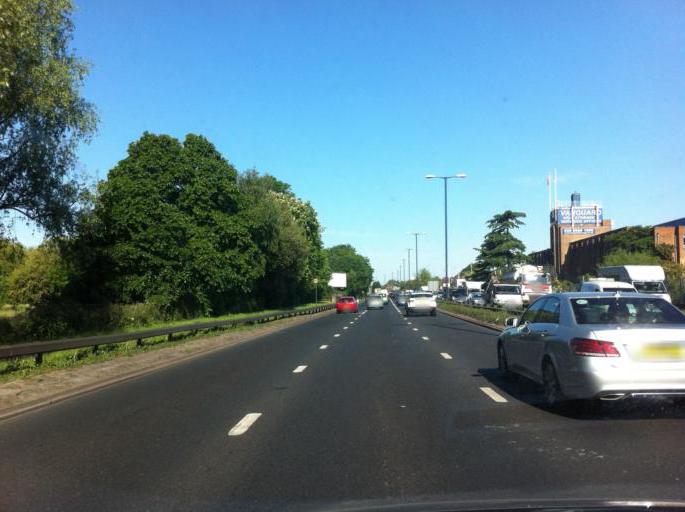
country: GB
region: England
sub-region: Greater London
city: Ealing Broadway
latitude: 51.5313
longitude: -0.3054
